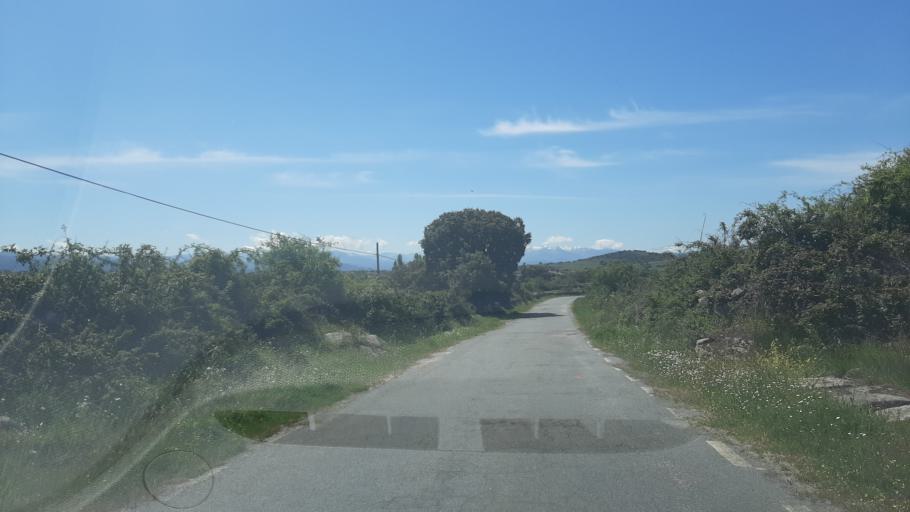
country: ES
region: Castille and Leon
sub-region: Provincia de Avila
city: Narrillos del Alamo
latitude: 40.5509
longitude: -5.4429
